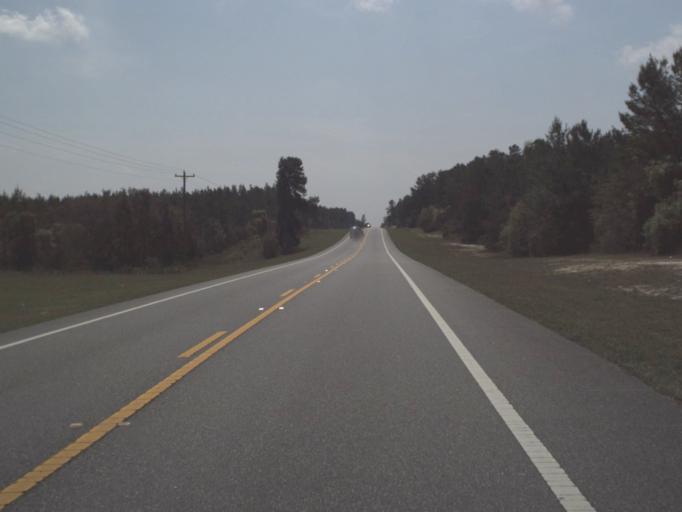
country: US
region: Florida
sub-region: Lake County
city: Astor
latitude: 29.1558
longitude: -81.6361
